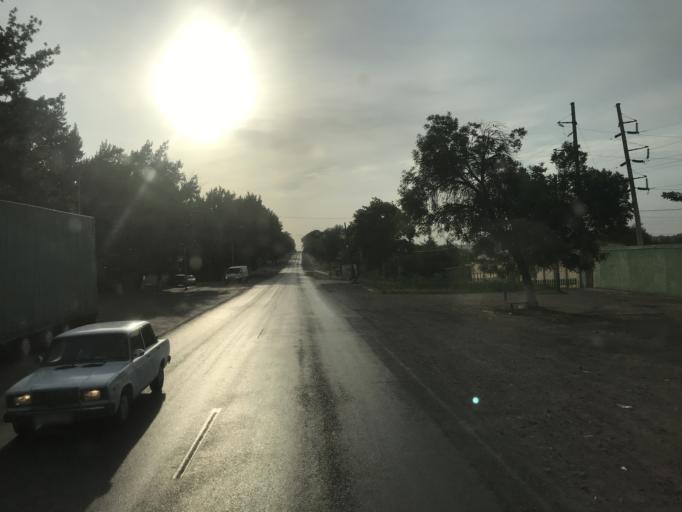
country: KZ
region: Ongtustik Qazaqstan
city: Saryaghash
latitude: 41.4907
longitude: 69.2759
